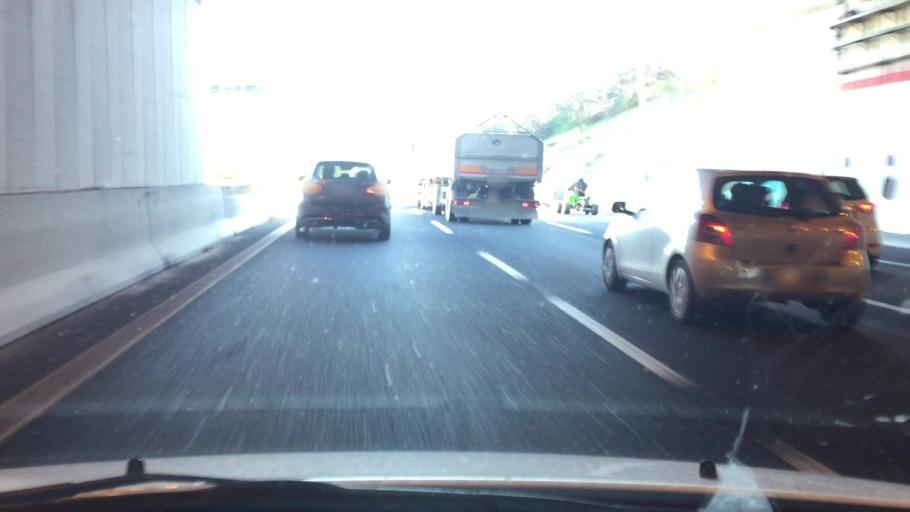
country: VA
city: Vatican City
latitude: 41.9810
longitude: 12.4360
